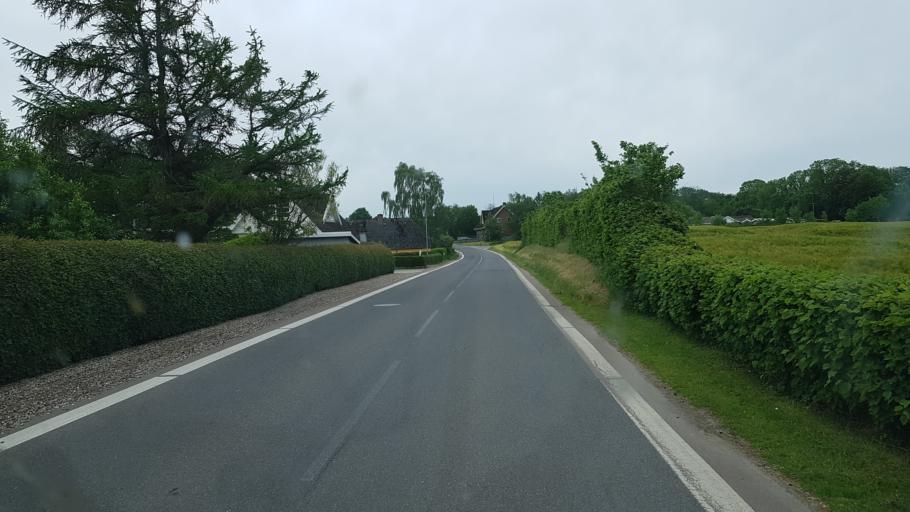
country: DK
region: South Denmark
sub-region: Middelfart Kommune
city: Brenderup
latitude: 55.4471
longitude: 10.0193
